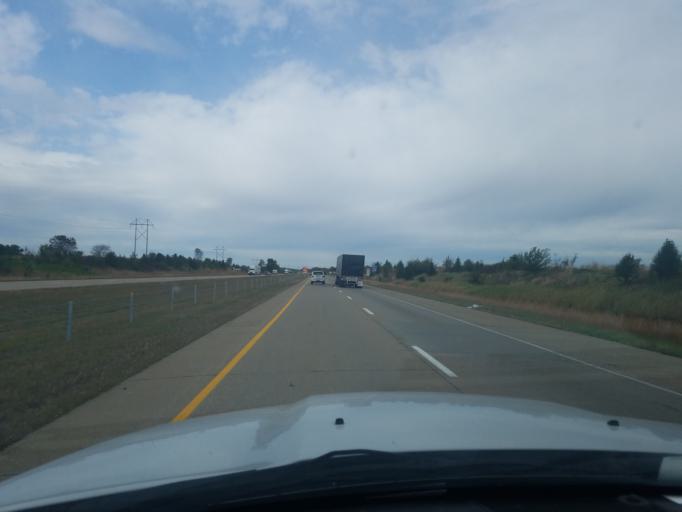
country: US
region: Indiana
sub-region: Vanderburgh County
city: Melody Hill
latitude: 38.0963
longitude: -87.4765
